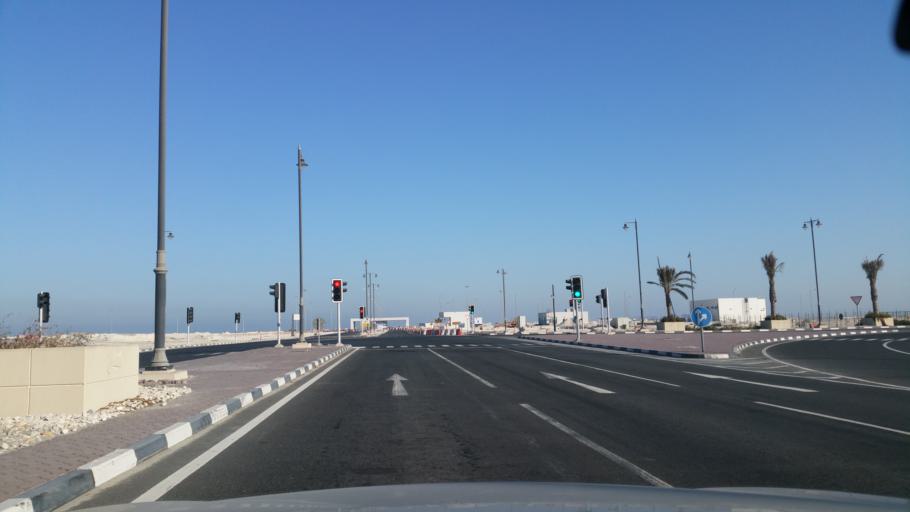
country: QA
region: Al Wakrah
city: Umm Sa'id
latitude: 25.0551
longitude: 51.6012
